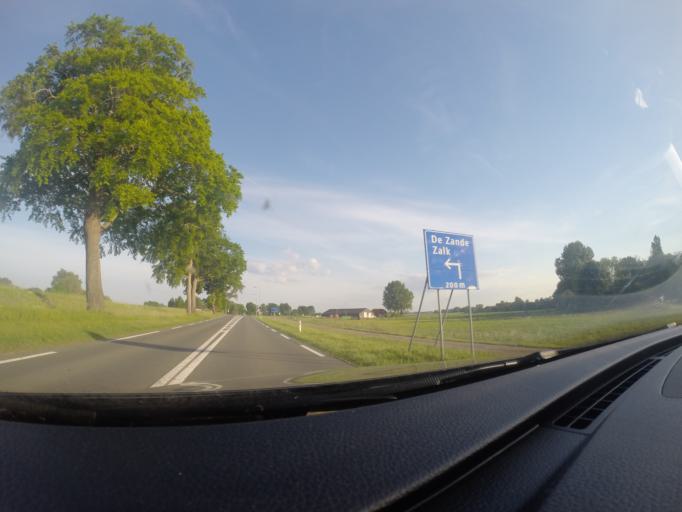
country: NL
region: Overijssel
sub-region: Gemeente Kampen
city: Kampen
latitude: 52.5202
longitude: 5.9556
